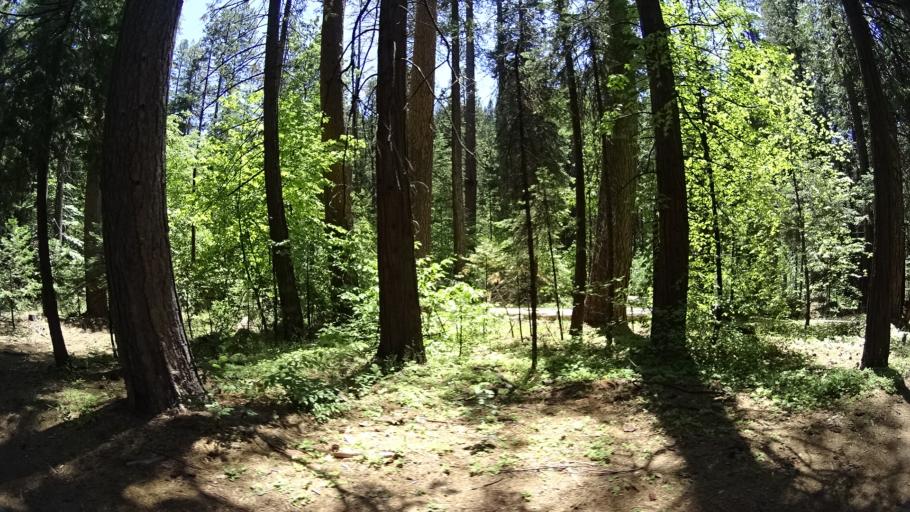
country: US
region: California
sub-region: Calaveras County
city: Arnold
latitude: 38.2462
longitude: -120.3072
